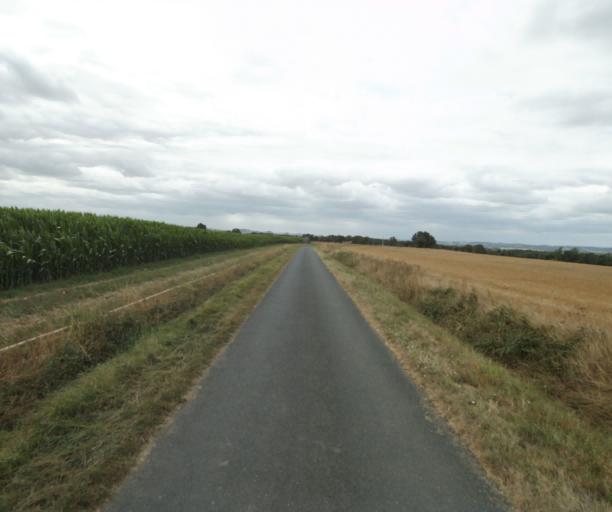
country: FR
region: Midi-Pyrenees
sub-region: Departement du Tarn
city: Soreze
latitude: 43.4736
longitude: 2.0514
